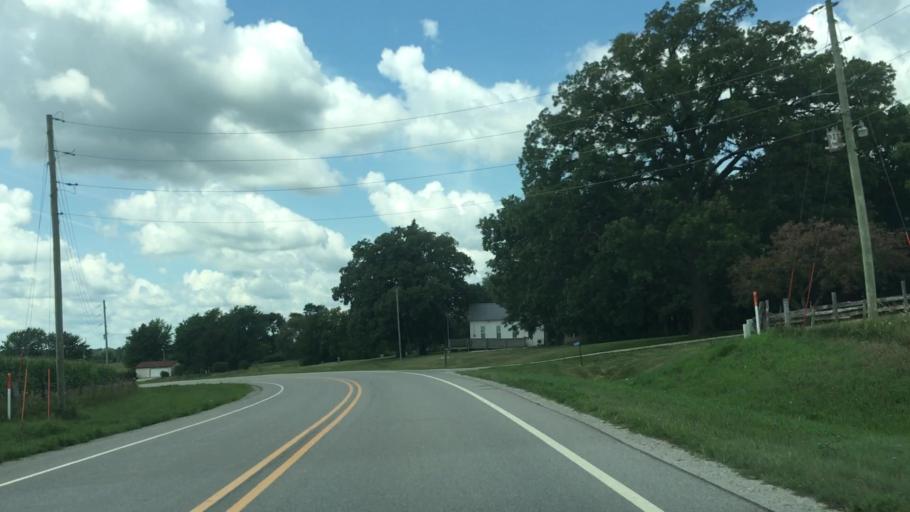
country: US
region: Iowa
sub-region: Johnson County
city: Solon
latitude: 41.8421
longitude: -91.4226
